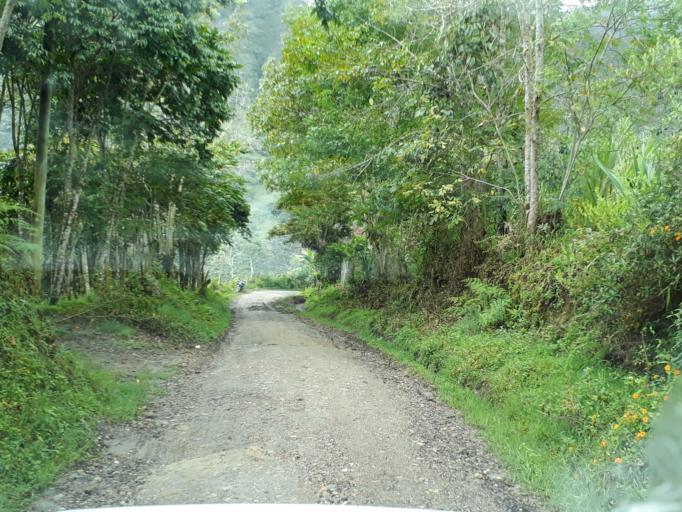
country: CO
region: Cundinamarca
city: Gacheta
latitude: 4.8556
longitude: -73.6470
